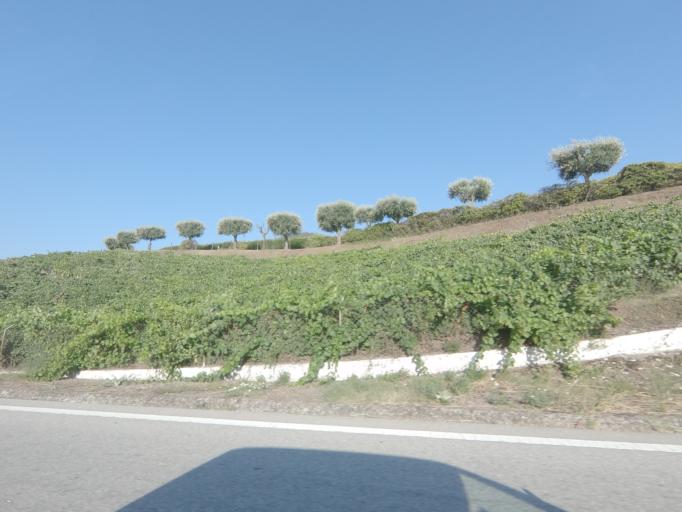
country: PT
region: Viseu
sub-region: Armamar
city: Armamar
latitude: 41.1477
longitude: -7.6862
